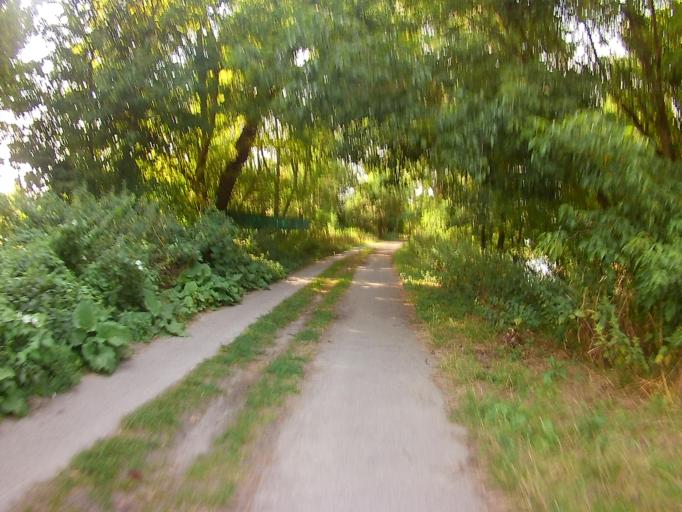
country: DE
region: Berlin
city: Biesdorf
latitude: 52.4788
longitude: 13.5635
